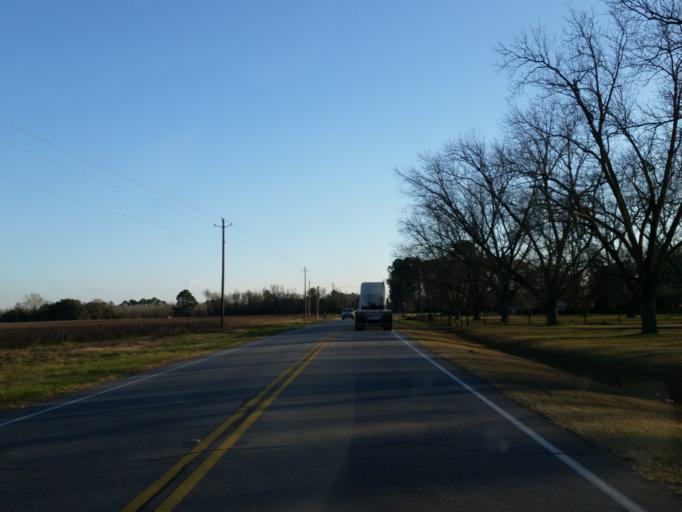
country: US
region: Georgia
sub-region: Dooly County
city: Vienna
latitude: 32.1128
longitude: -83.7982
